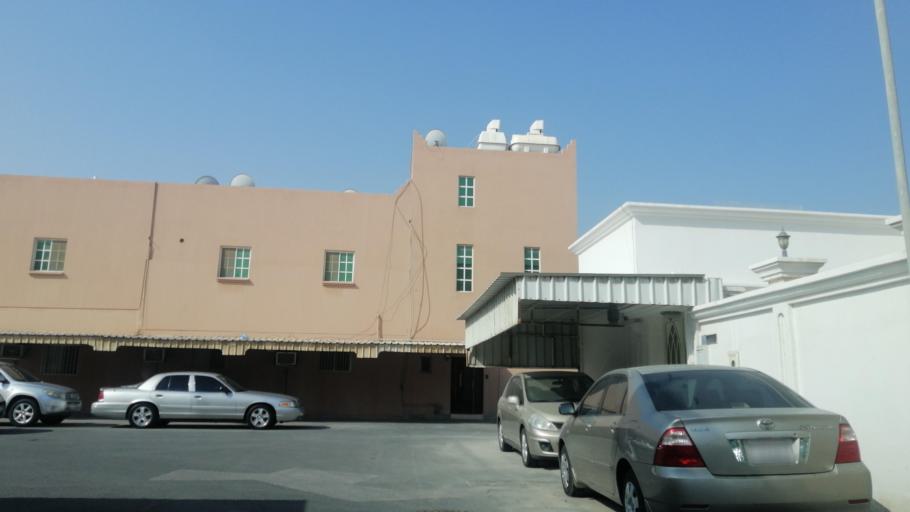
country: BH
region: Muharraq
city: Al Muharraq
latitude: 26.2577
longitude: 50.6348
